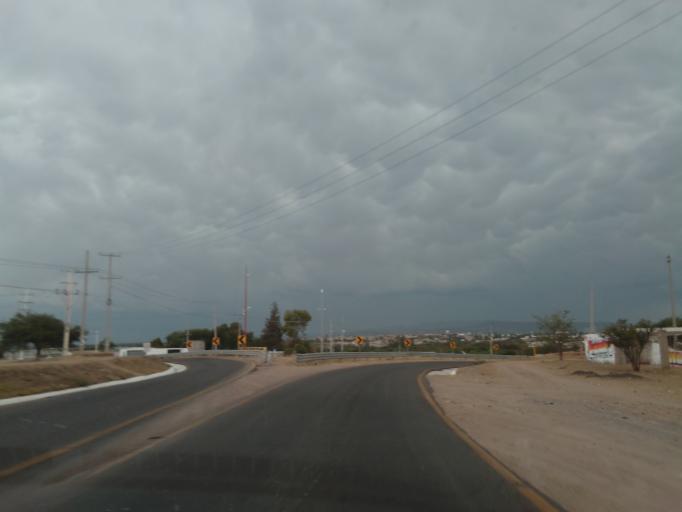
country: MX
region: Guanajuato
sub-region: Dolores Hidalgo Cuna de la Independencia Nacional
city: Ejido Jesus Maria
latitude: 21.1701
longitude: -100.8885
